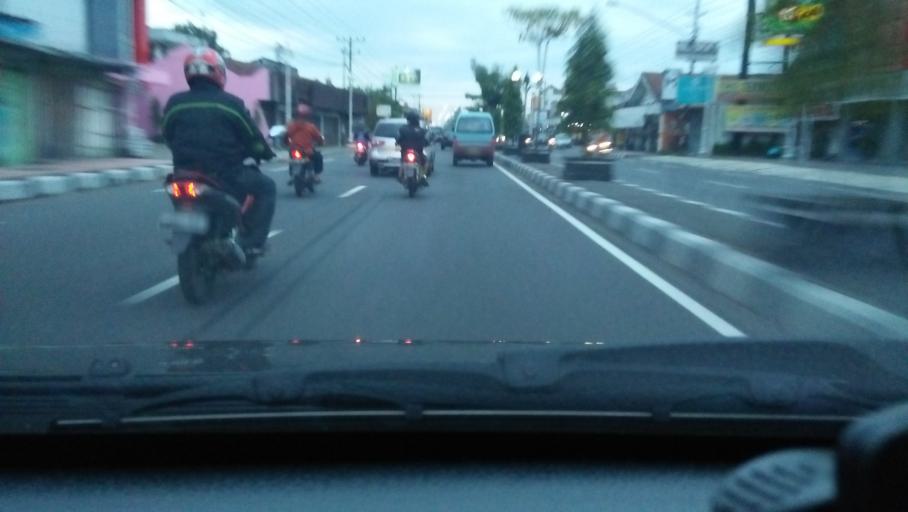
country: ID
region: Central Java
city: Mertoyudan
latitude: -7.5115
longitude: 110.2252
